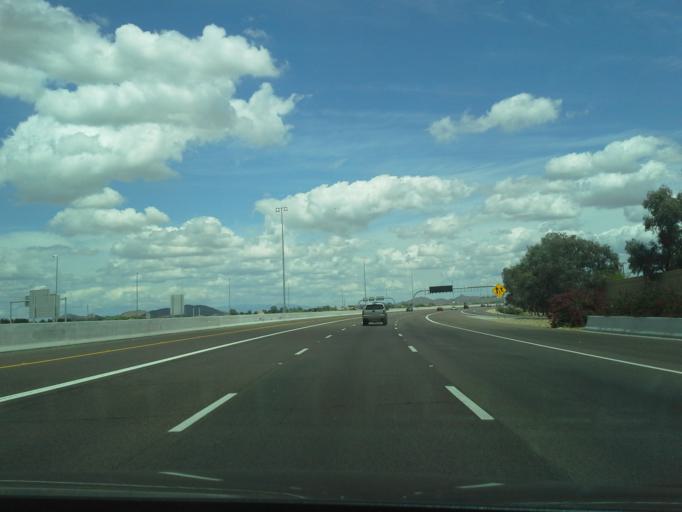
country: US
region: Arizona
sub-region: Maricopa County
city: Sun City
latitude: 33.6588
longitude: -112.2322
